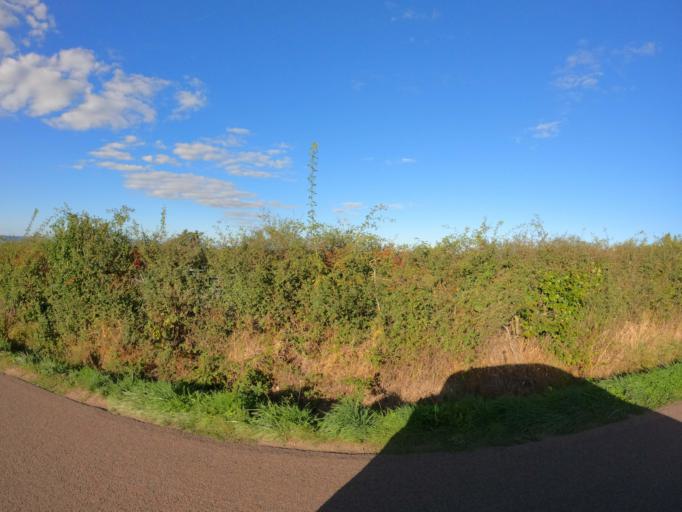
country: FR
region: Bourgogne
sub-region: Departement de Saone-et-Loire
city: Ecuisses
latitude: 46.7390
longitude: 4.5498
